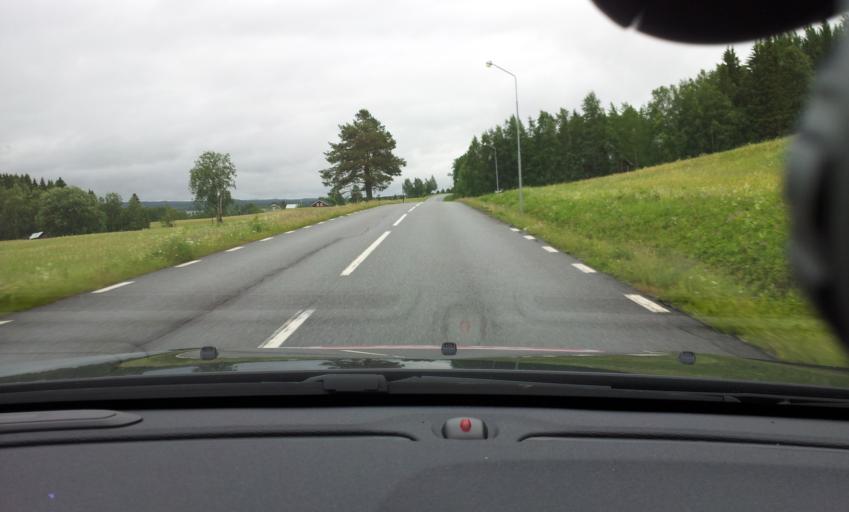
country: SE
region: Jaemtland
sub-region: Stroemsunds Kommun
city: Stroemsund
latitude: 63.5690
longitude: 15.3889
